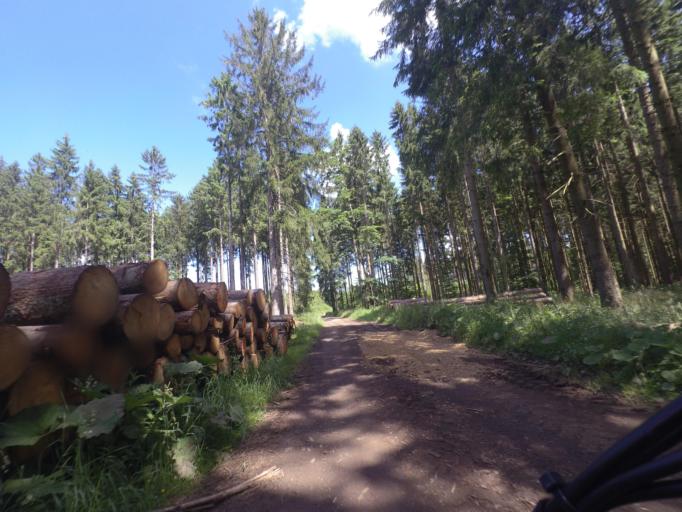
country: DE
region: Rheinland-Pfalz
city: Junkerath
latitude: 50.3156
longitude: 6.5596
